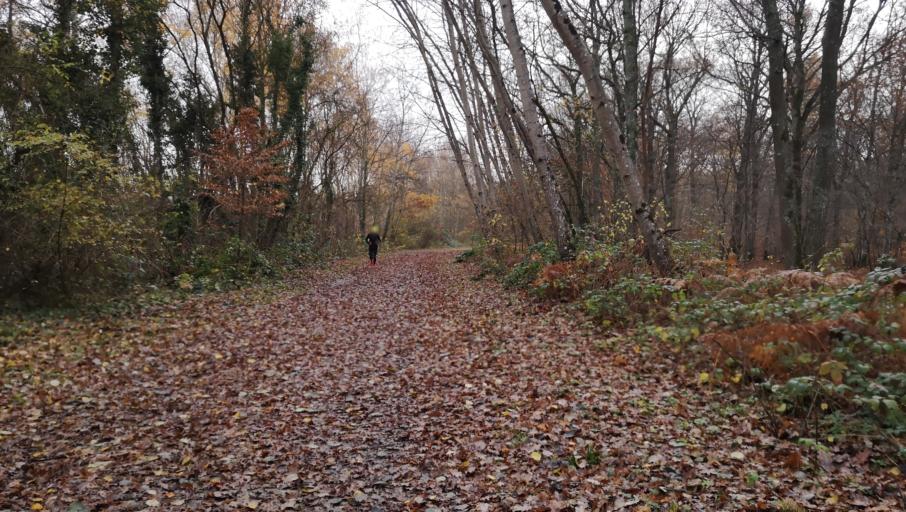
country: FR
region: Centre
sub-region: Departement du Loiret
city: Boigny-sur-Bionne
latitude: 47.9413
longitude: 2.0028
